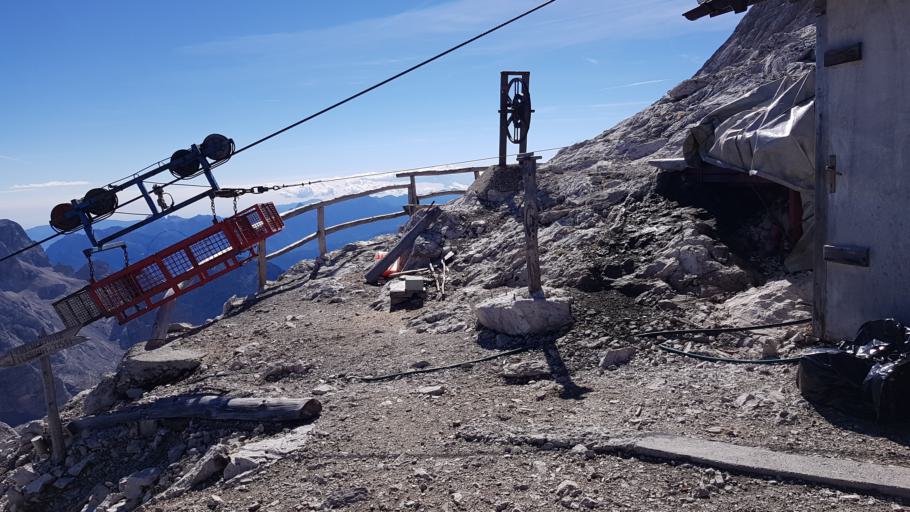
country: IT
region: Veneto
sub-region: Provincia di Belluno
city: Alleghe
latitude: 46.3785
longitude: 12.0567
